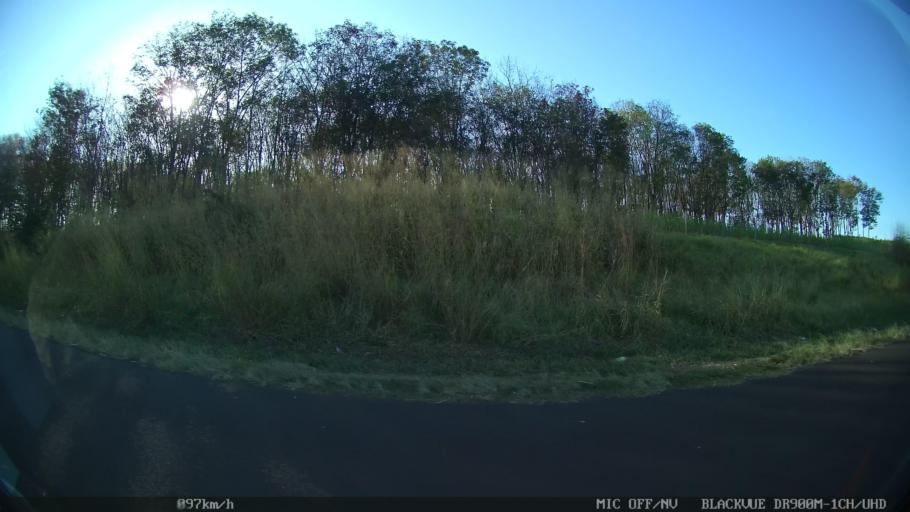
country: BR
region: Sao Paulo
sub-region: Guapiacu
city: Guapiacu
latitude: -20.7653
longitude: -49.1948
